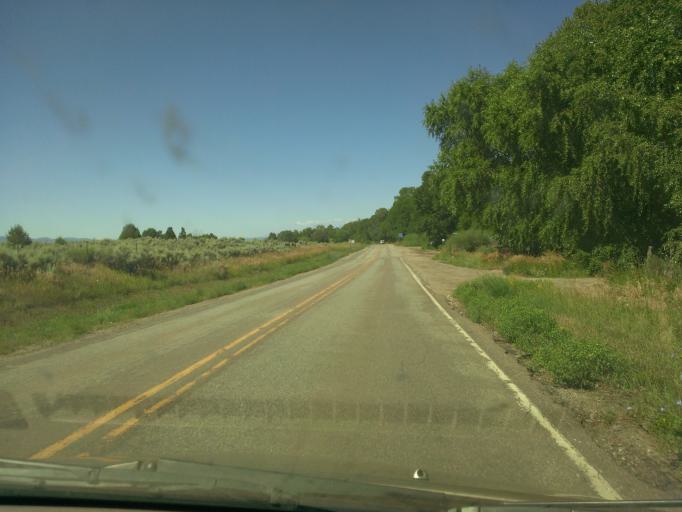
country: US
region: New Mexico
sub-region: Taos County
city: Arroyo Seco
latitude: 36.5115
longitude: -105.5794
